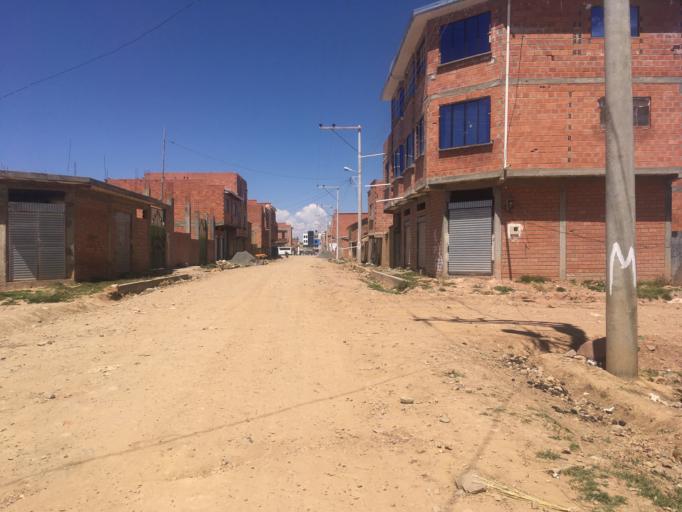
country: BO
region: La Paz
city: Huatajata
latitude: -16.1891
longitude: -68.7441
